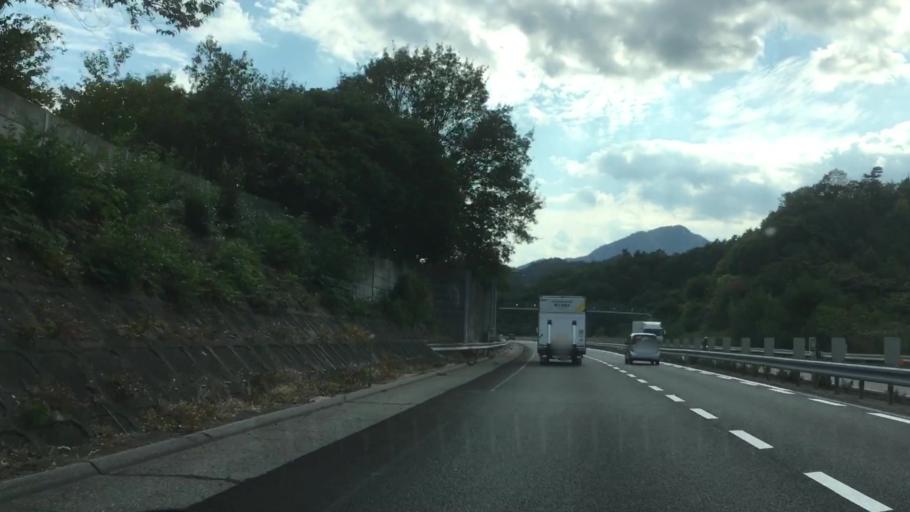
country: JP
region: Hiroshima
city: Ono-hara
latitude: 34.3198
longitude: 132.2844
